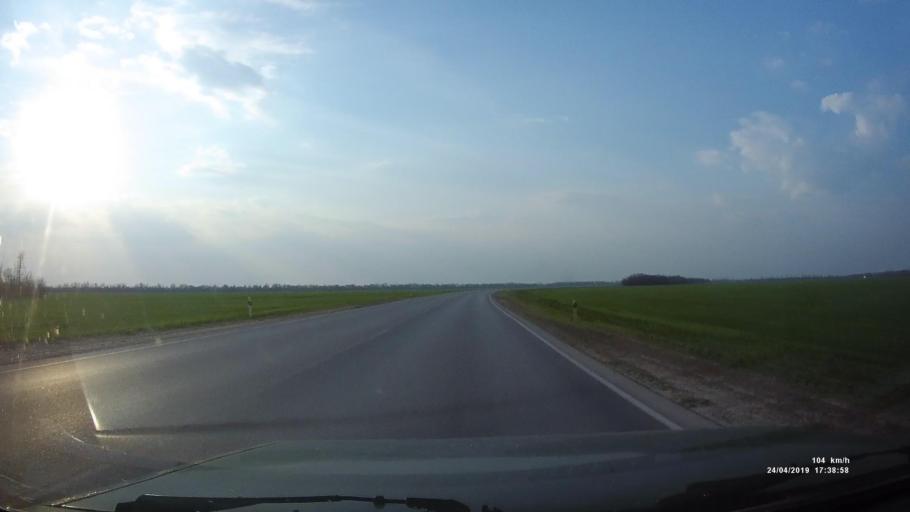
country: RU
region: Rostov
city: Tselina
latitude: 46.5159
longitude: 40.9964
